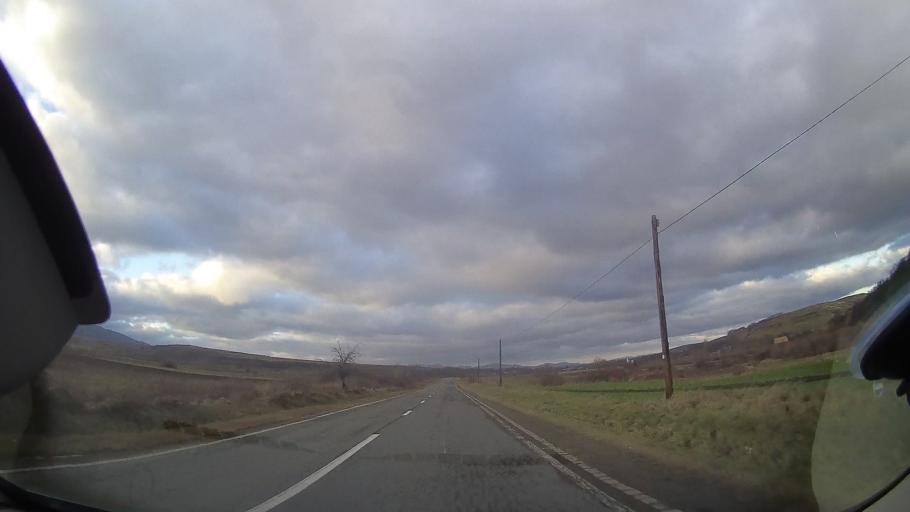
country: RO
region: Cluj
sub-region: Comuna Calatele
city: Calatele
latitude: 46.7887
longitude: 22.9991
